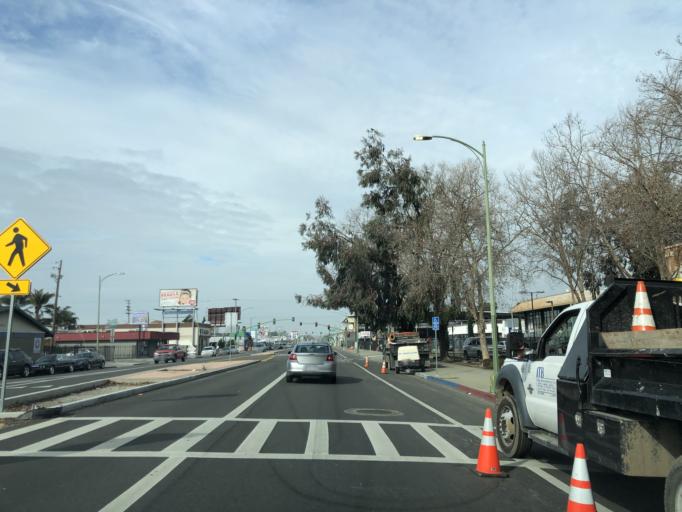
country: US
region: California
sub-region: Alameda County
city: San Leandro
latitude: 37.7380
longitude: -122.1657
